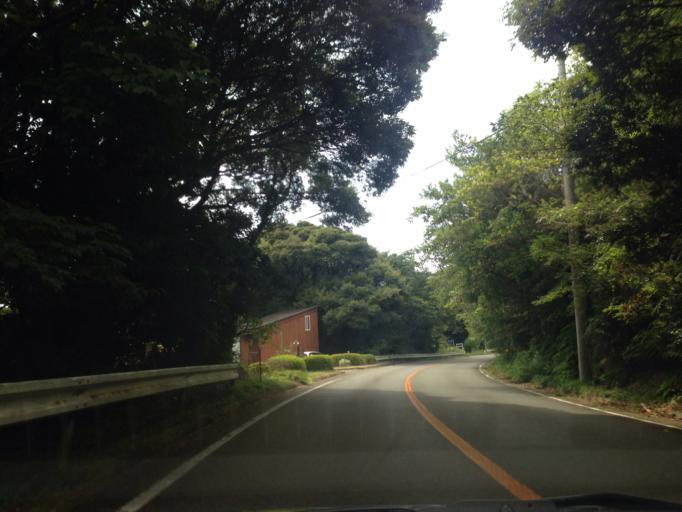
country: JP
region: Shizuoka
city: Shimoda
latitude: 34.6939
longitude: 138.7672
